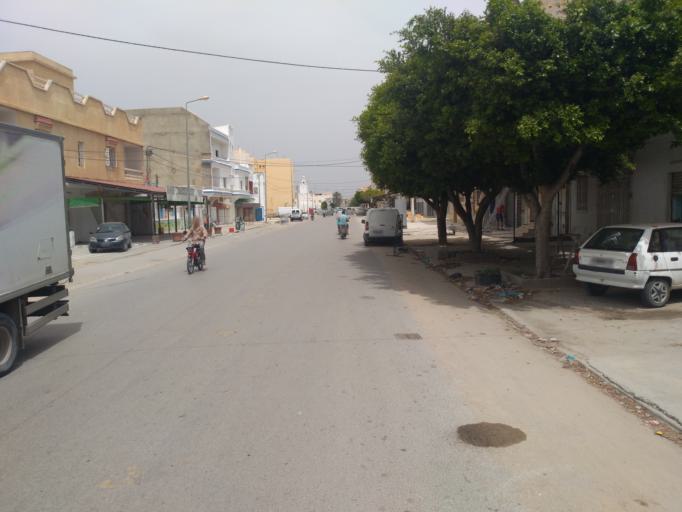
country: TN
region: Al Qayrawan
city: Kairouan
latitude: 35.6695
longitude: 10.0888
